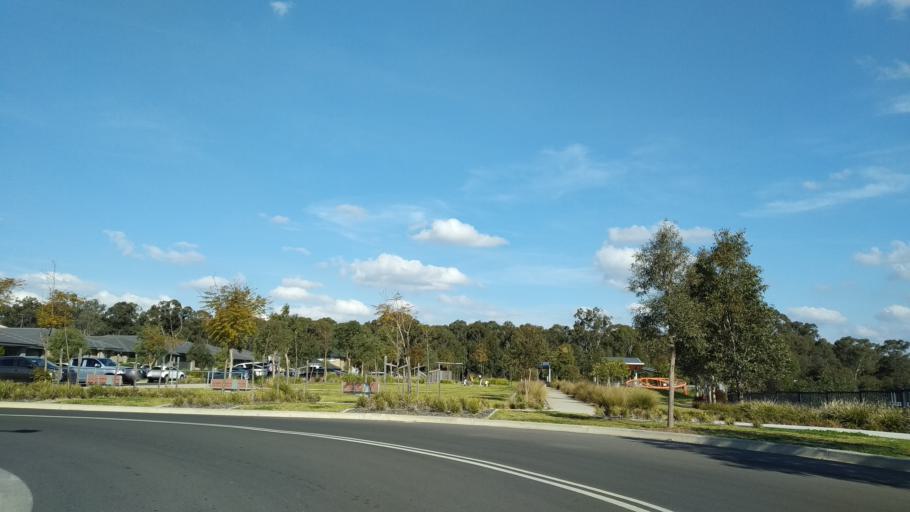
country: AU
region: New South Wales
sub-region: Blacktown
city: Hassall Grove
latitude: -33.7238
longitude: 150.8492
